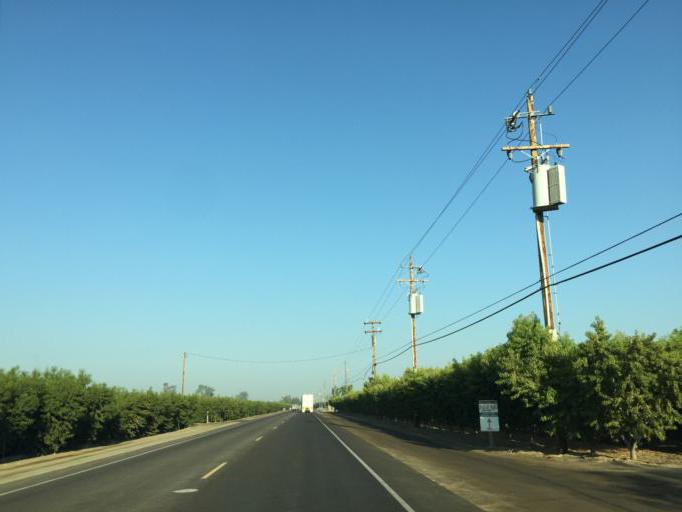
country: US
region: California
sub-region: Fresno County
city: Kingsburg
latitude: 36.4887
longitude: -119.5025
